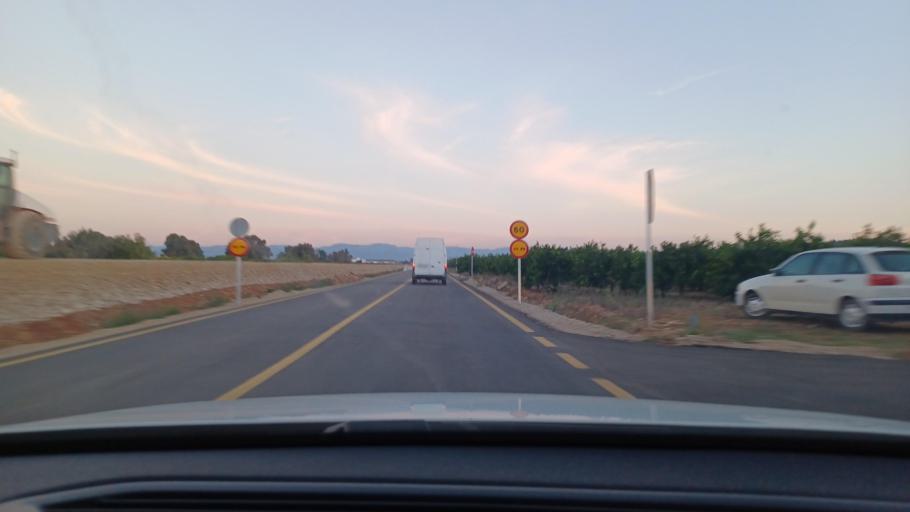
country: ES
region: Catalonia
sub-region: Provincia de Tarragona
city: Alcanar
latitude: 40.5356
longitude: 0.4421
